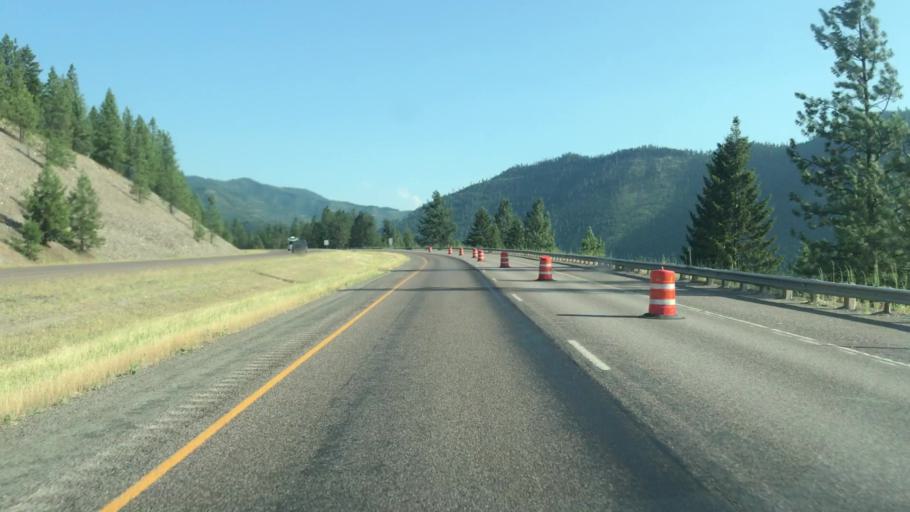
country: US
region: Montana
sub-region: Mineral County
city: Superior
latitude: 47.0196
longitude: -114.7365
